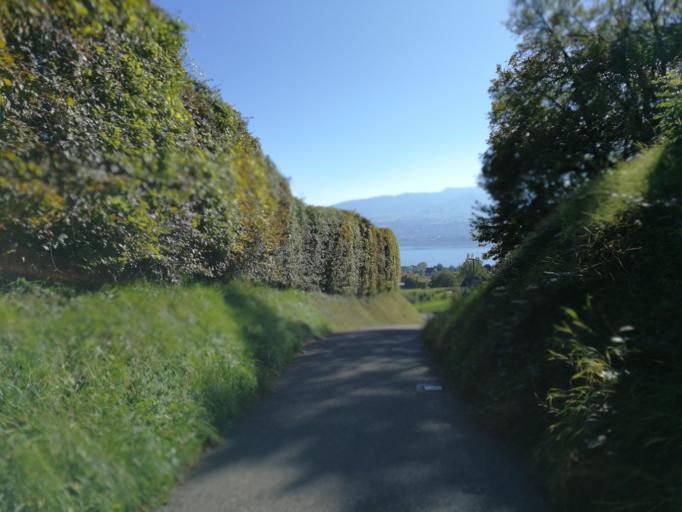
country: CH
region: Zurich
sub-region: Bezirk Meilen
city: Stafa
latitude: 47.2487
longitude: 8.7160
